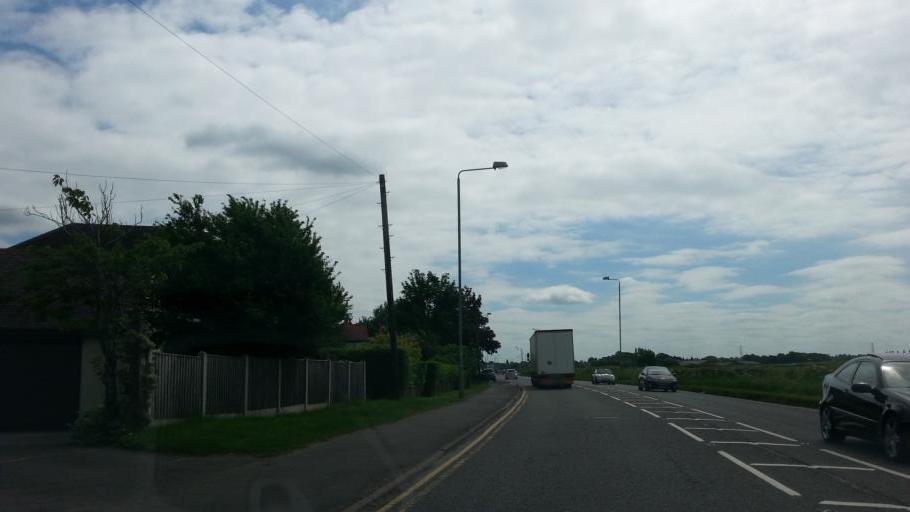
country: GB
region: England
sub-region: Nottinghamshire
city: West Bridgford
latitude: 52.8992
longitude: -1.1006
